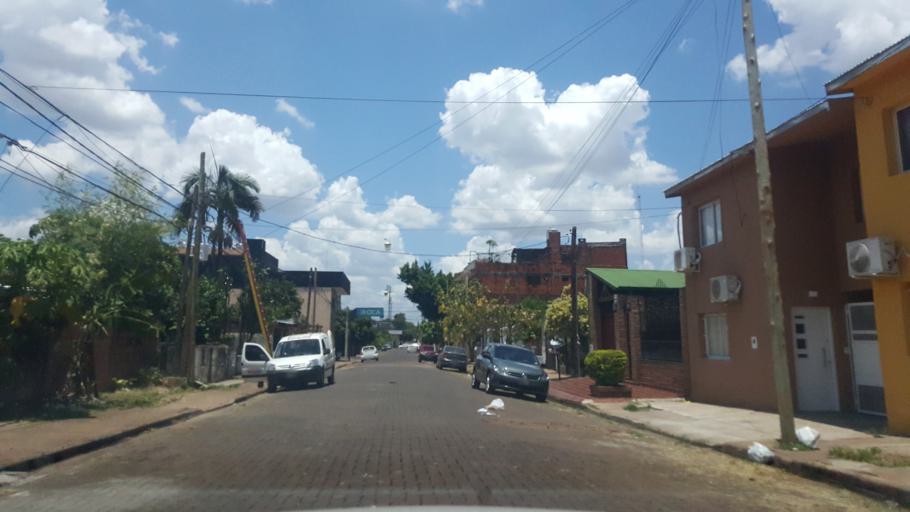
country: AR
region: Misiones
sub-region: Departamento de Capital
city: Posadas
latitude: -27.3857
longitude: -55.9024
